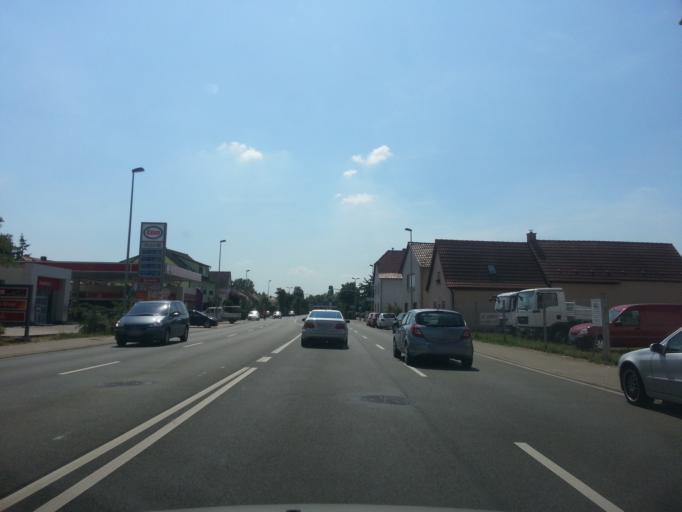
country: DE
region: Hesse
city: Lampertheim
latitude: 49.5949
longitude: 8.4623
